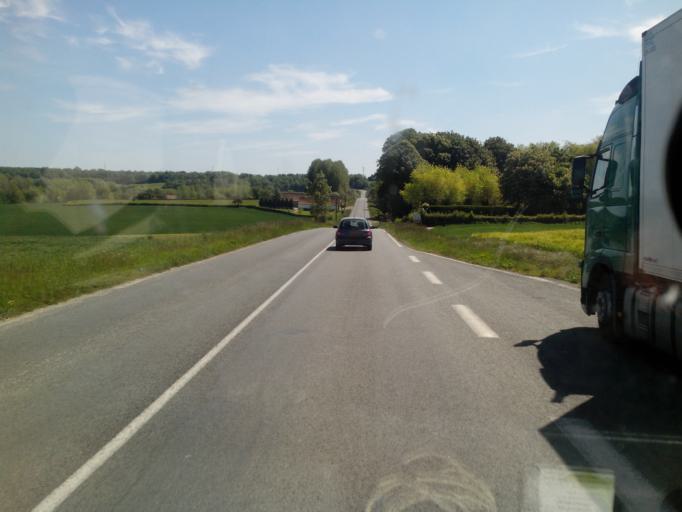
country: FR
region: Nord-Pas-de-Calais
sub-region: Departement du Pas-de-Calais
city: Samer
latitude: 50.6220
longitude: 1.7413
